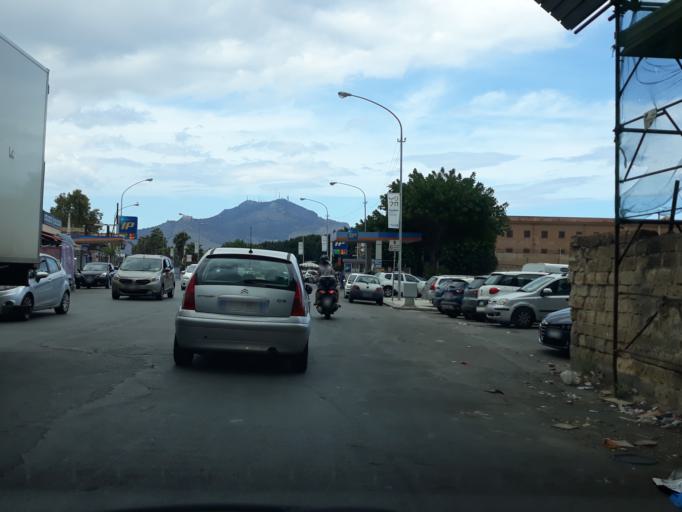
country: IT
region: Sicily
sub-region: Palermo
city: Ciaculli
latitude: 38.1119
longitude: 13.3784
